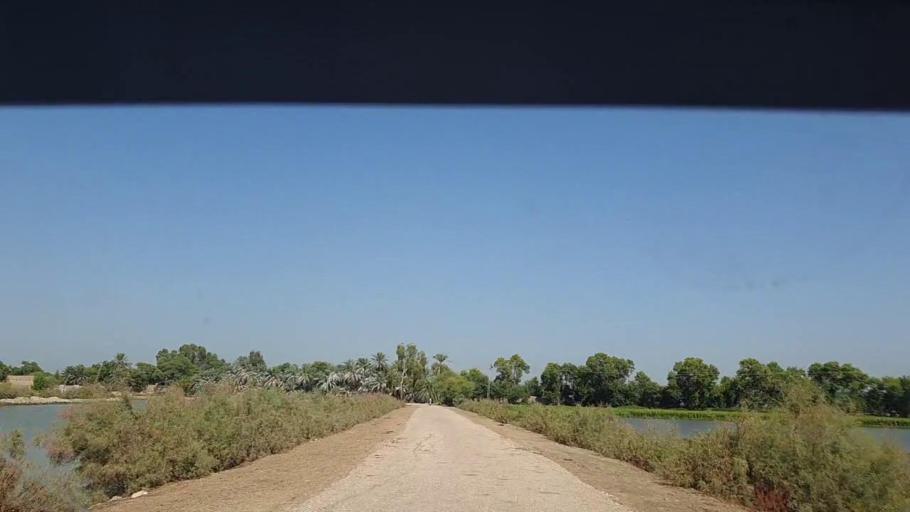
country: PK
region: Sindh
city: Ghauspur
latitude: 28.2030
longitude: 69.0437
